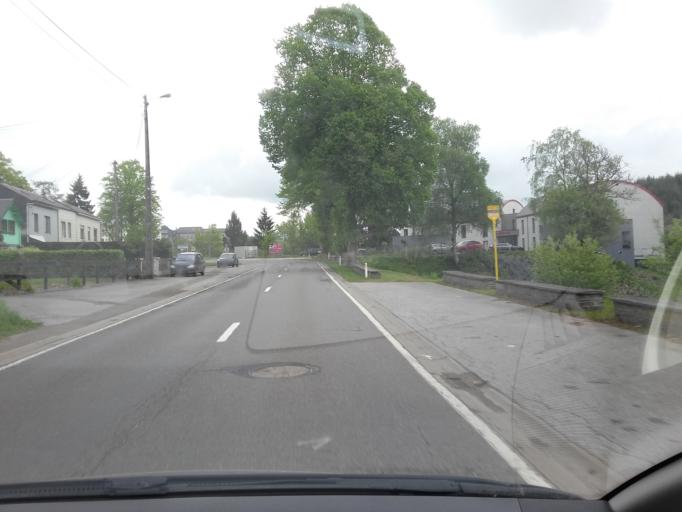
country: BE
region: Wallonia
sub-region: Province du Luxembourg
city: Neufchateau
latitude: 49.8376
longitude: 5.4276
